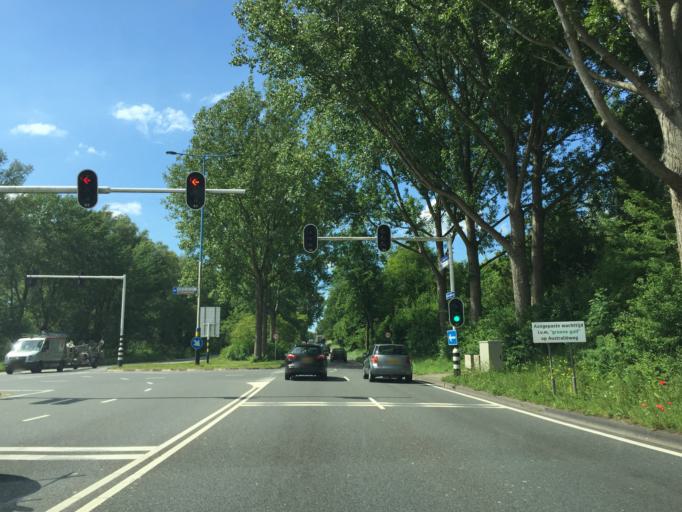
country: NL
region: South Holland
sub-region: Gemeente Zoetermeer
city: Zoetermeer
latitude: 52.0578
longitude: 4.5128
